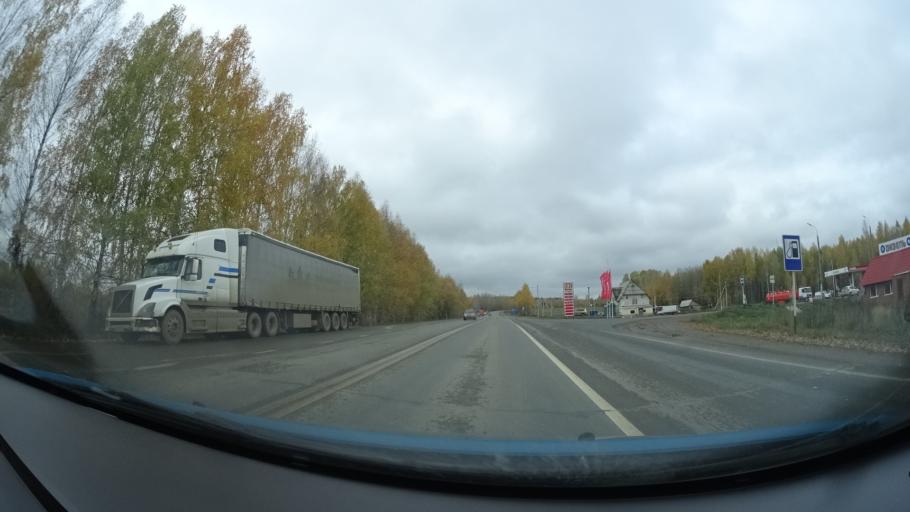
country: RU
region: Perm
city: Osa
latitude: 57.1793
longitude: 55.5401
